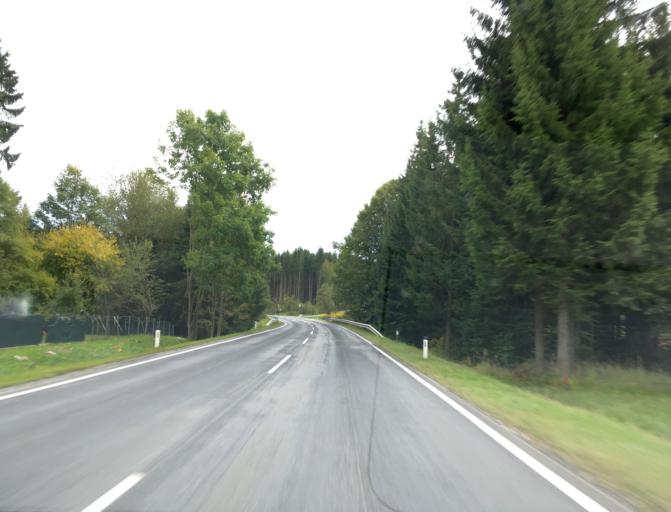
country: AT
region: Lower Austria
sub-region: Politischer Bezirk Neunkirchen
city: Thomasberg
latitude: 47.5388
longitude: 16.1596
